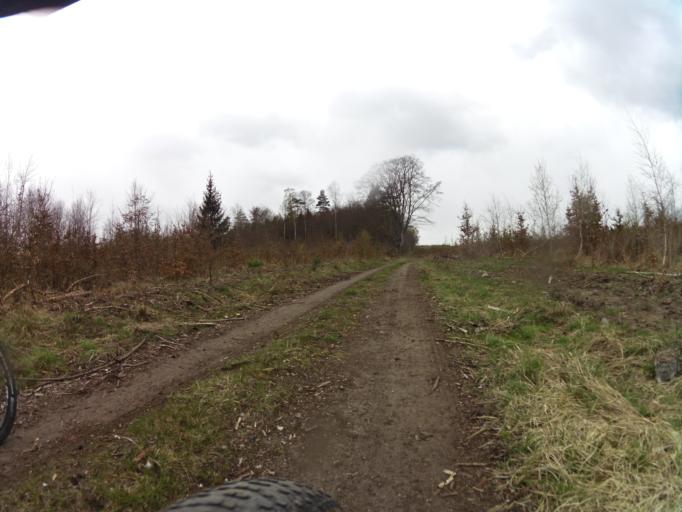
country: PL
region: West Pomeranian Voivodeship
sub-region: Powiat koszalinski
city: Polanow
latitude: 54.0770
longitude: 16.6158
